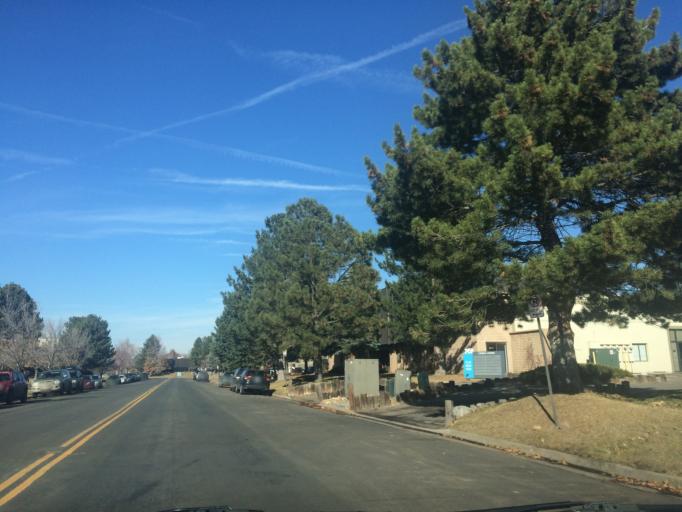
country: US
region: Colorado
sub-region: Boulder County
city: Boulder
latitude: 40.0234
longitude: -105.2183
